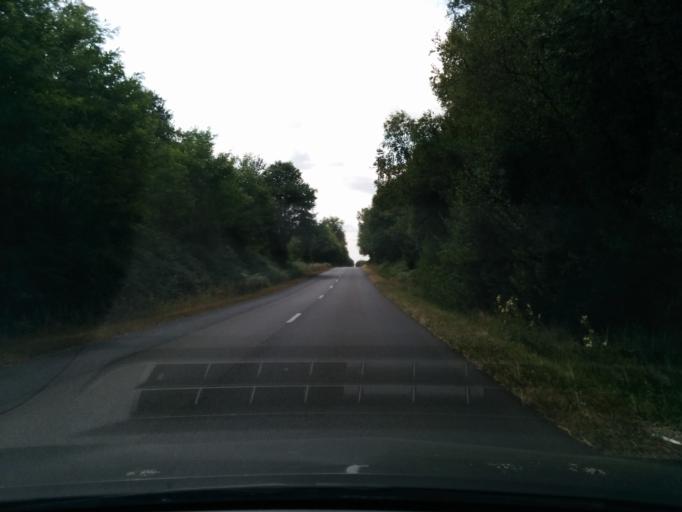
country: FR
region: Centre
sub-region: Departement du Cher
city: Neuvy-sur-Barangeon
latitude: 47.3246
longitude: 2.3204
